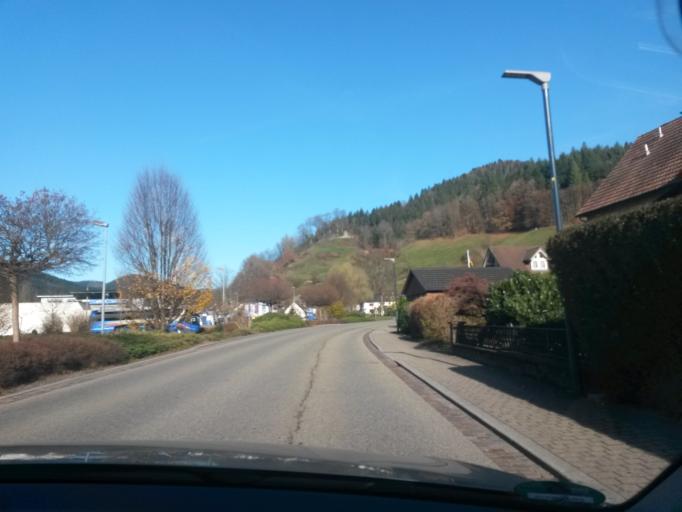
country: DE
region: Baden-Wuerttemberg
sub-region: Freiburg Region
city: Oberwolfach
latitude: 48.3076
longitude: 8.2196
